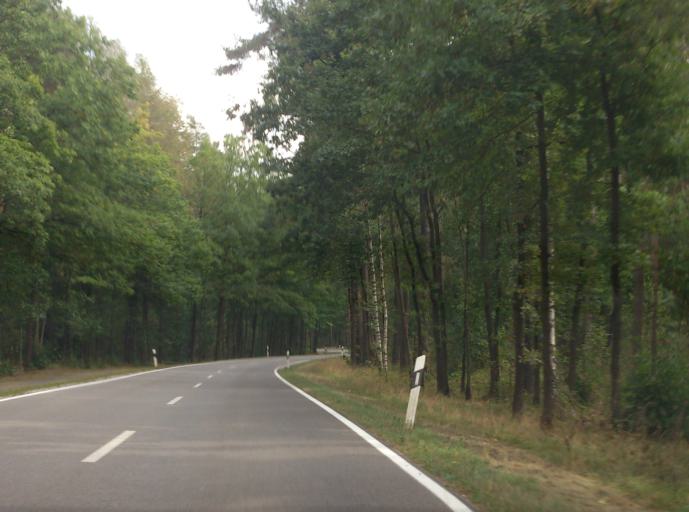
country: DE
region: Bavaria
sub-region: Regierungsbezirk Mittelfranken
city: Wetzendorf
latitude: 49.5287
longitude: 11.0678
